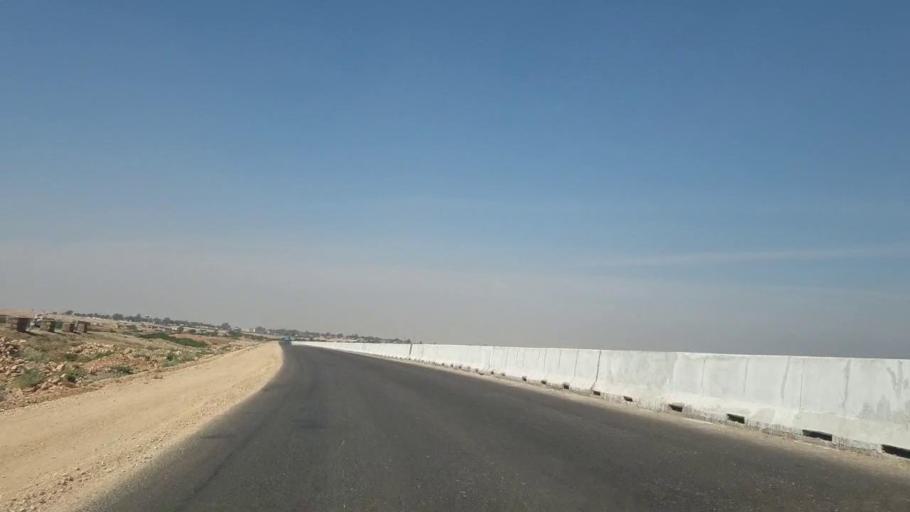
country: PK
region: Sindh
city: Matiari
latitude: 25.6564
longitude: 68.3000
